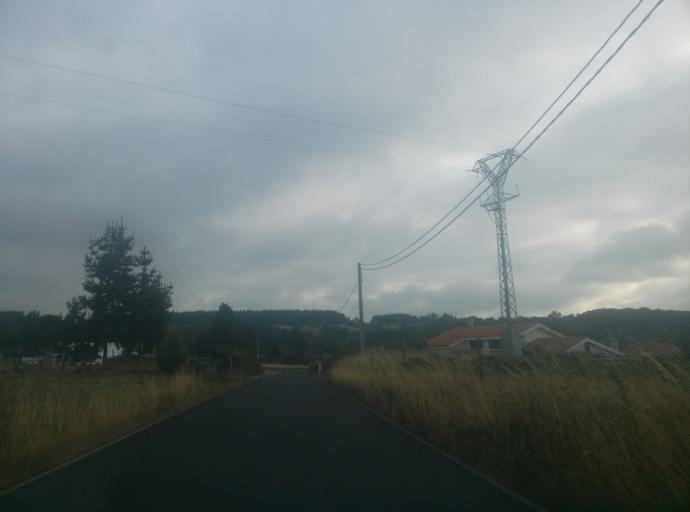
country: ES
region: Galicia
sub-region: Provincia de Lugo
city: Outeiro de Rei
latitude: 43.0863
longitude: -7.5469
